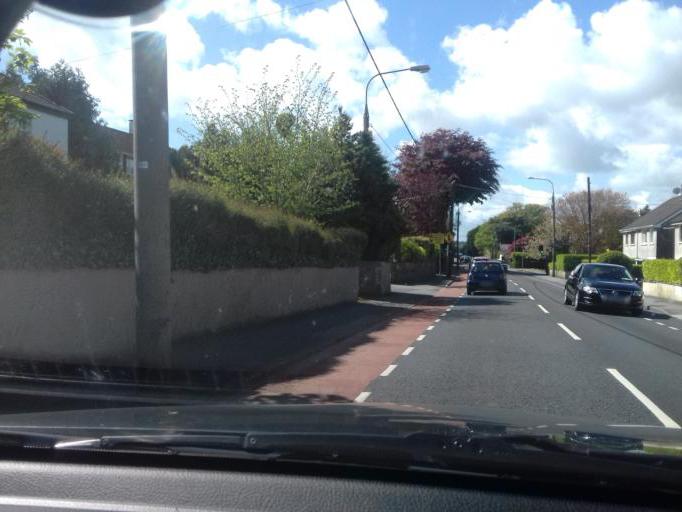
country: IE
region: Munster
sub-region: Waterford
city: Waterford
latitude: 52.2487
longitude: -7.0889
